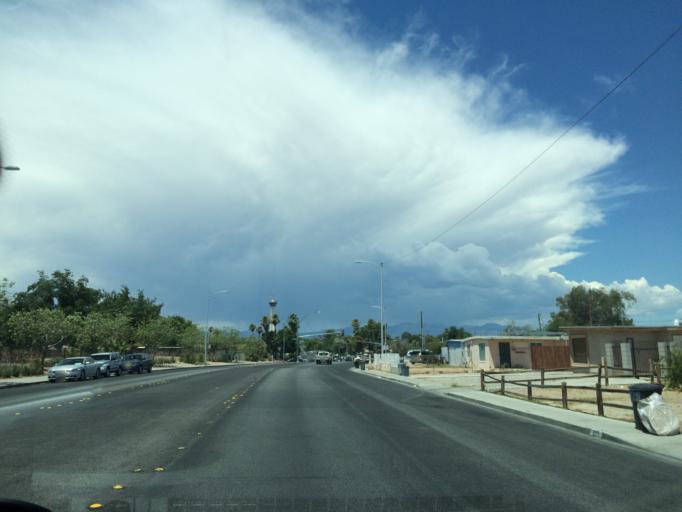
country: US
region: Nevada
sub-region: Clark County
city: Winchester
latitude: 36.1481
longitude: -115.1170
